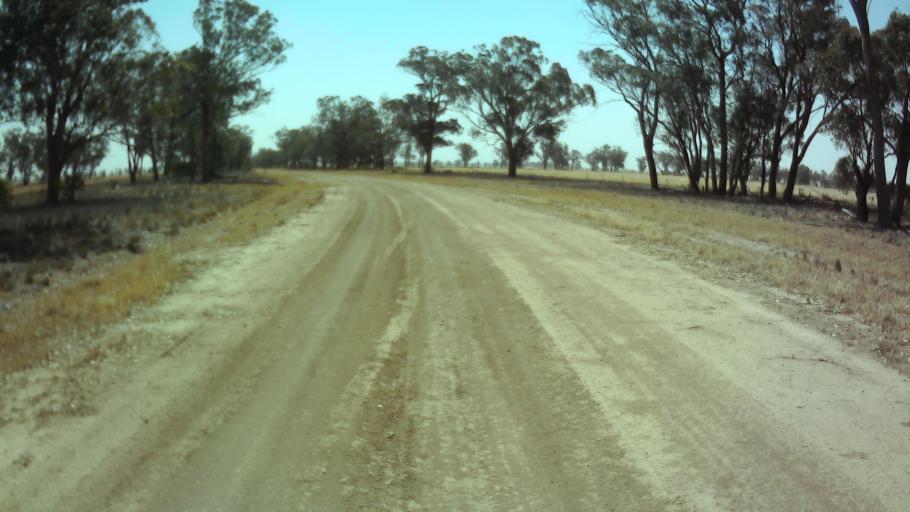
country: AU
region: New South Wales
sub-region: Weddin
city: Grenfell
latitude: -33.9358
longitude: 147.8062
